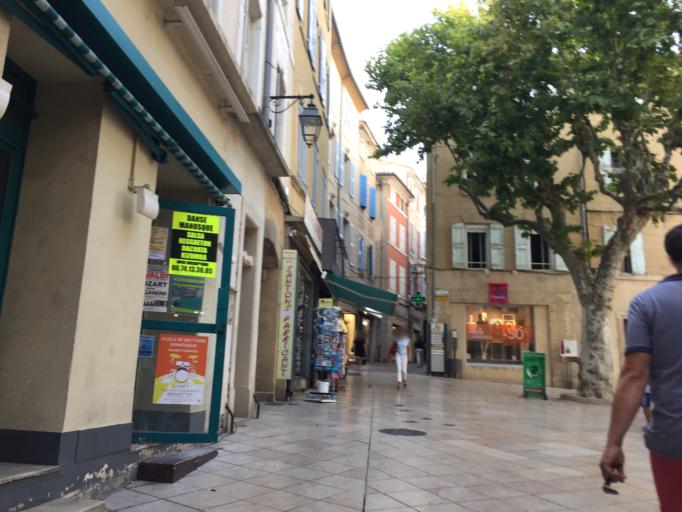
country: FR
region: Provence-Alpes-Cote d'Azur
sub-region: Departement des Alpes-de-Haute-Provence
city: Manosque
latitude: 43.8325
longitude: 5.7834
